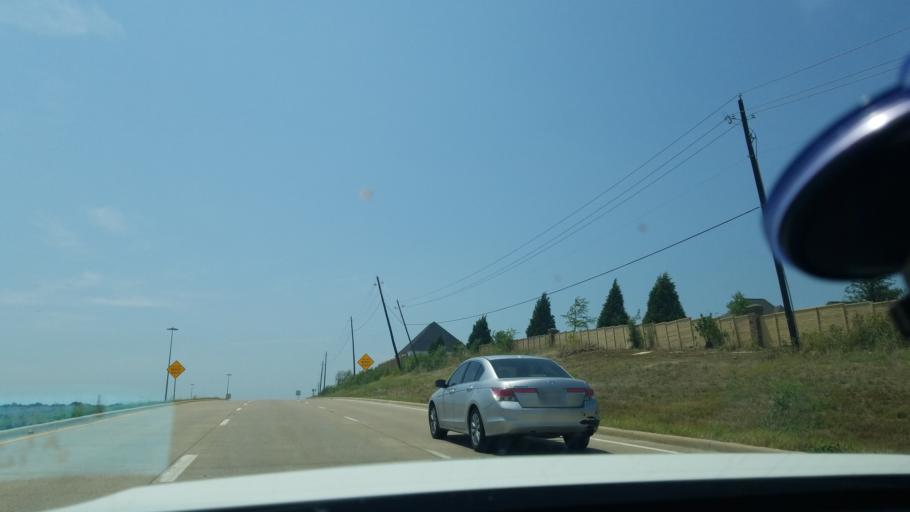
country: US
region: Texas
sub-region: Dallas County
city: Irving
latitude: 32.8754
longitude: -96.9943
